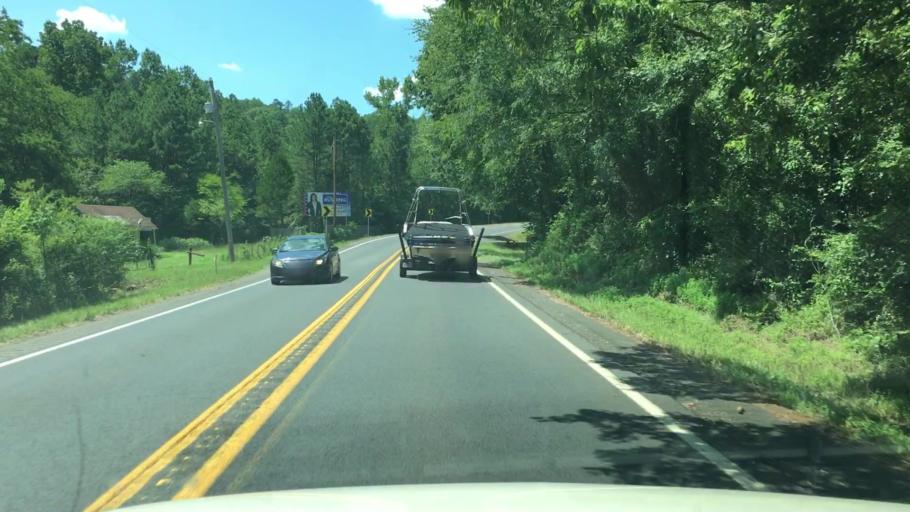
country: US
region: Arkansas
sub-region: Garland County
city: Lake Hamilton
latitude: 34.3395
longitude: -93.1821
